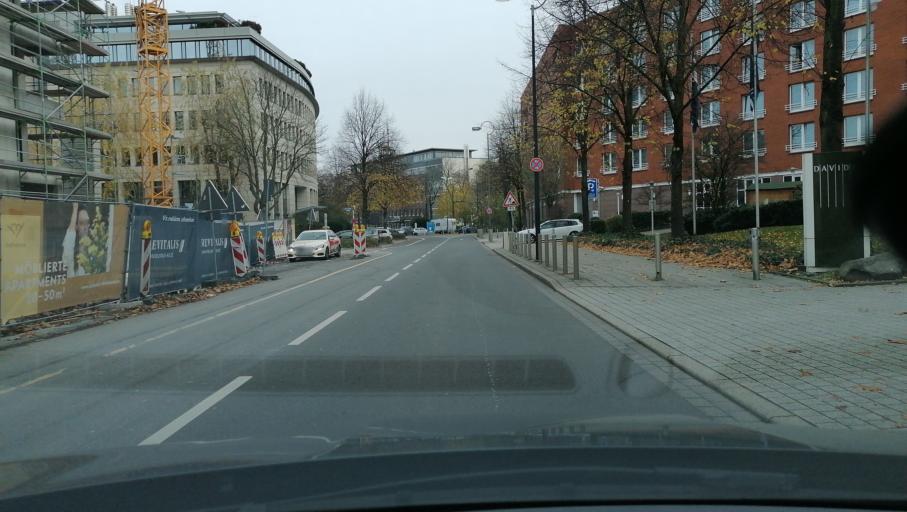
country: DE
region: North Rhine-Westphalia
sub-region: Regierungsbezirk Arnsberg
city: Dortmund
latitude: 51.4983
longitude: 7.4519
